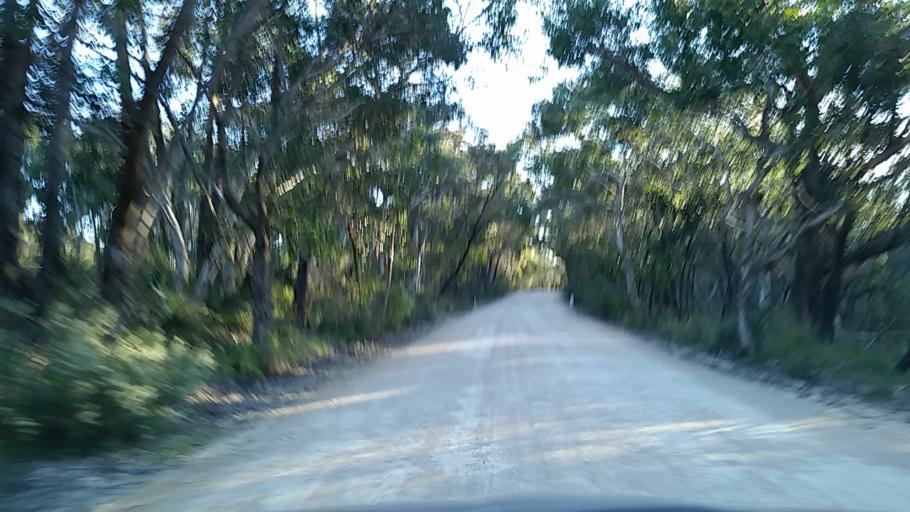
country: AU
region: South Australia
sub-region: Alexandrina
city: Mount Compass
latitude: -35.2995
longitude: 138.6818
